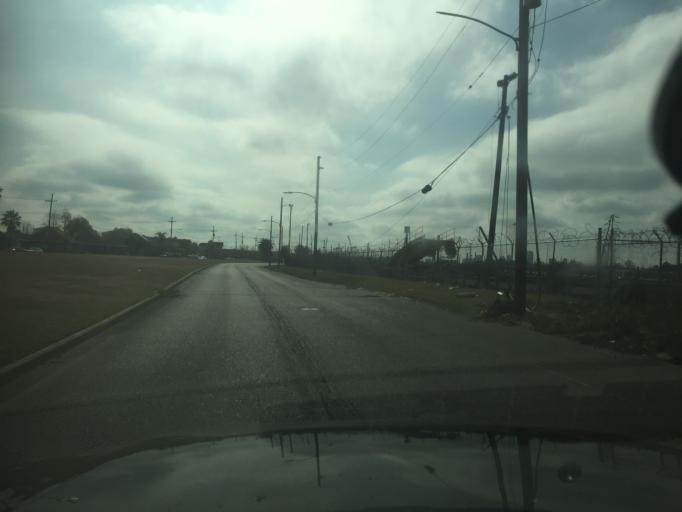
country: US
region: Louisiana
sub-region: Orleans Parish
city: New Orleans
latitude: 29.9979
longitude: -90.0419
